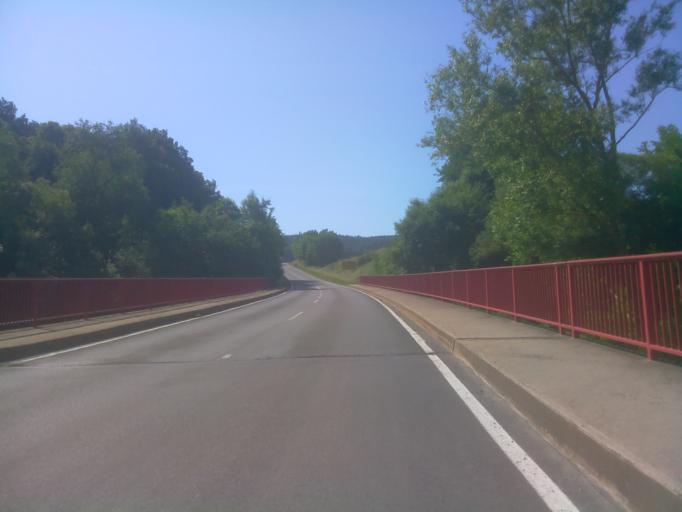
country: DE
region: Thuringia
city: Rudolstadt
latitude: 50.7189
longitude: 11.3984
